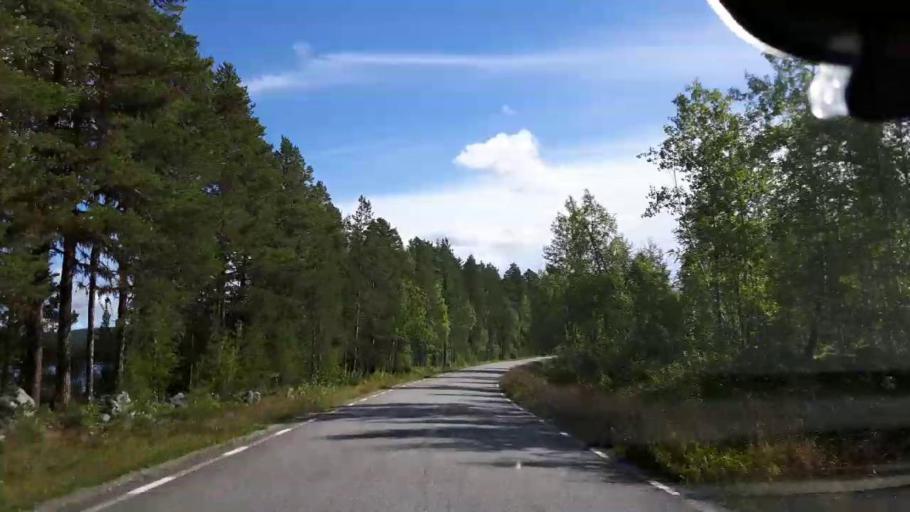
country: SE
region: Jaemtland
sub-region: Braecke Kommun
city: Braecke
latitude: 63.2238
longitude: 15.3029
